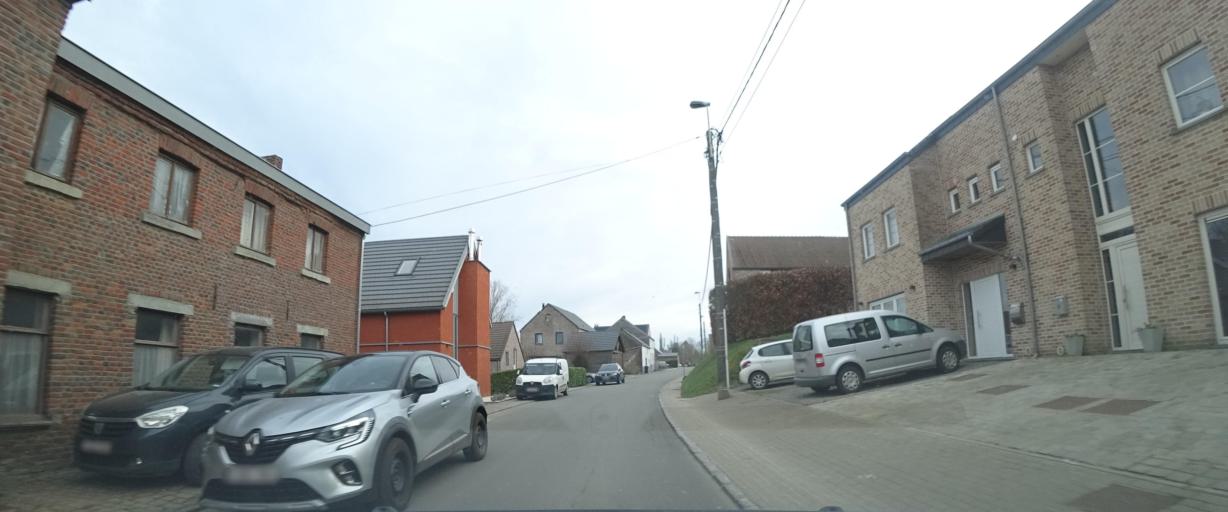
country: BE
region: Wallonia
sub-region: Province du Brabant Wallon
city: Chastre
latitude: 50.5958
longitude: 4.6046
